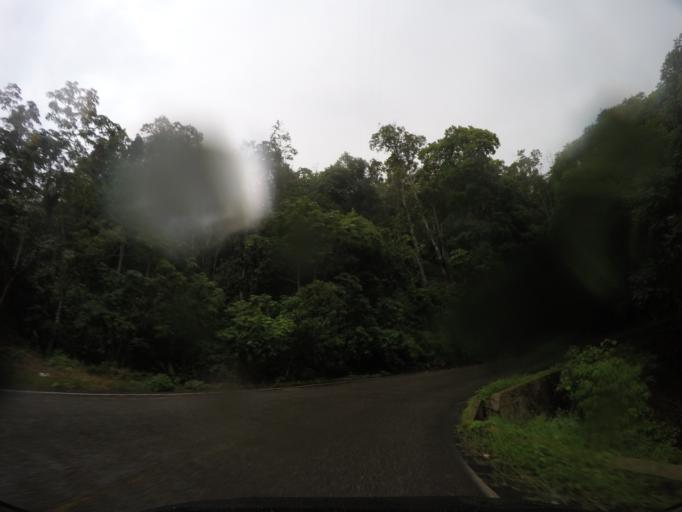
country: MX
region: Oaxaca
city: San Gabriel Mixtepec
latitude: 16.0811
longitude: -97.0790
